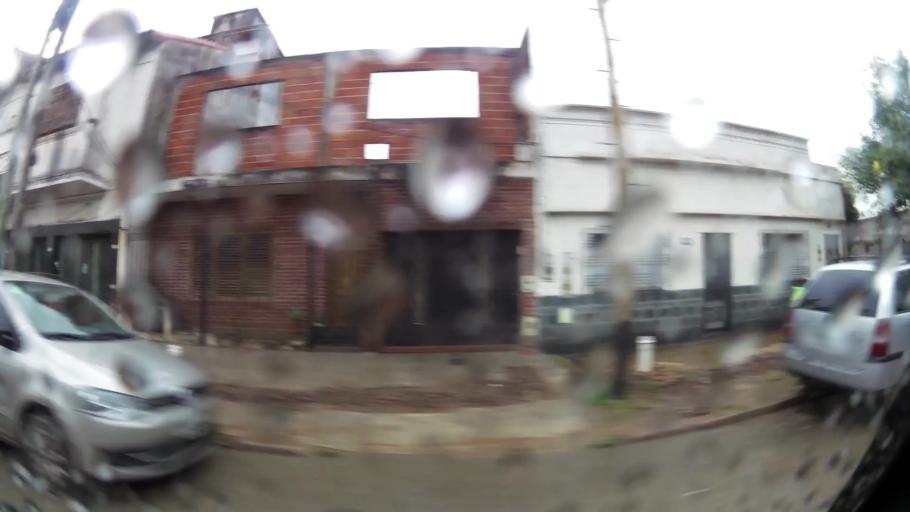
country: AR
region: Buenos Aires
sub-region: Partido de Lanus
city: Lanus
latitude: -34.7171
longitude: -58.3960
